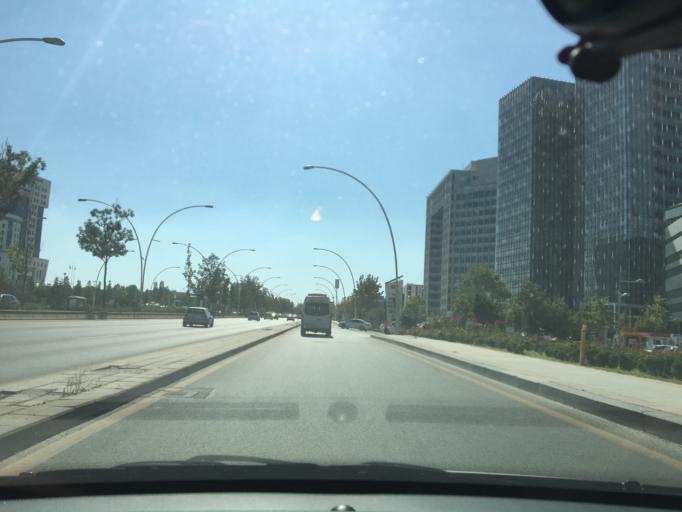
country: TR
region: Ankara
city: Batikent
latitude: 39.9076
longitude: 32.7553
